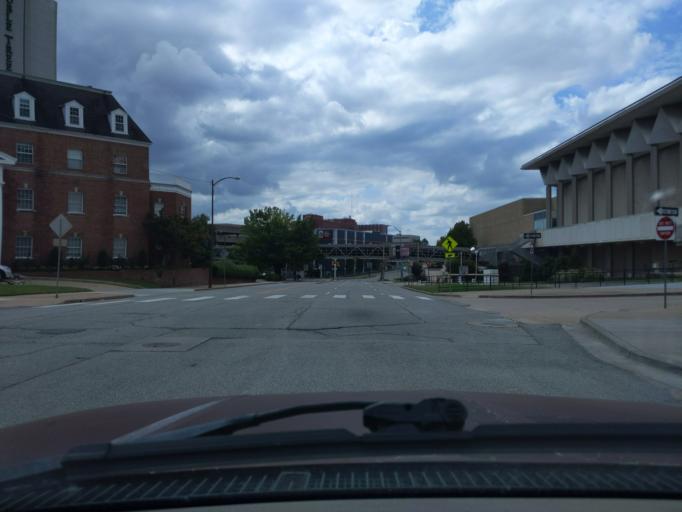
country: US
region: Oklahoma
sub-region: Tulsa County
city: Tulsa
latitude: 36.1485
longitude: -95.9954
